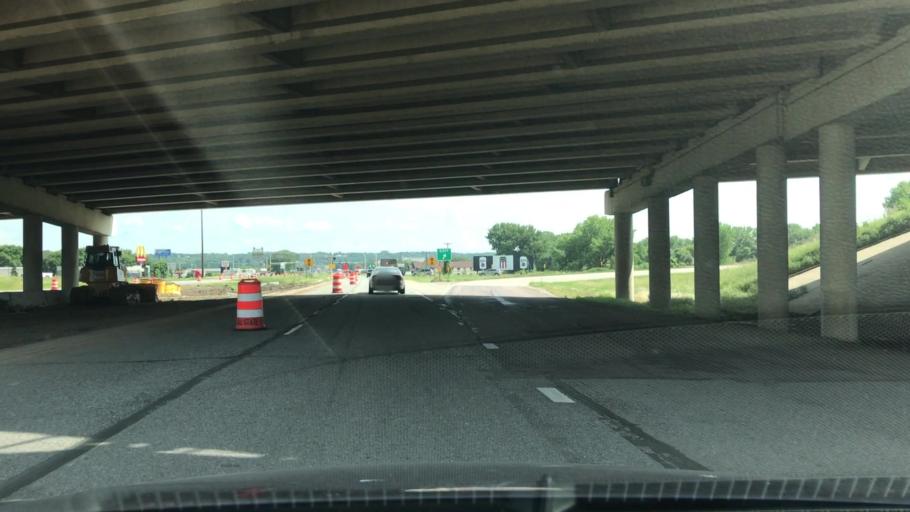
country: US
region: Minnesota
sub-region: Nicollet County
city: North Mankato
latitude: 44.1918
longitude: -94.0173
